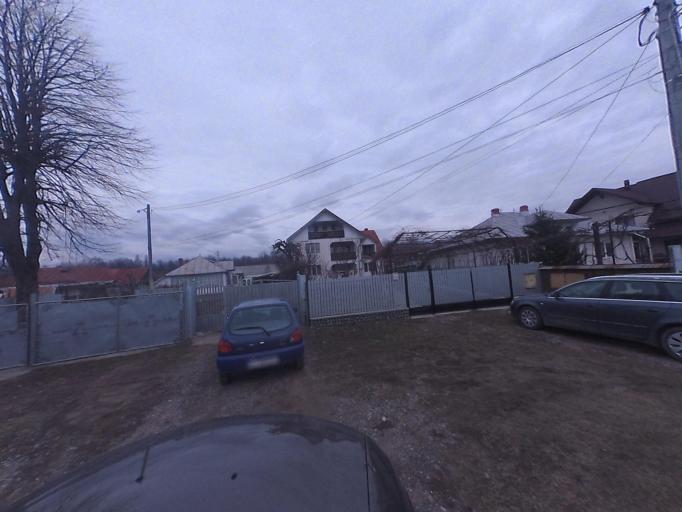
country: RO
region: Neamt
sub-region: Oras Targu Neamt
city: Targu Neamt
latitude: 47.2088
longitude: 26.3837
